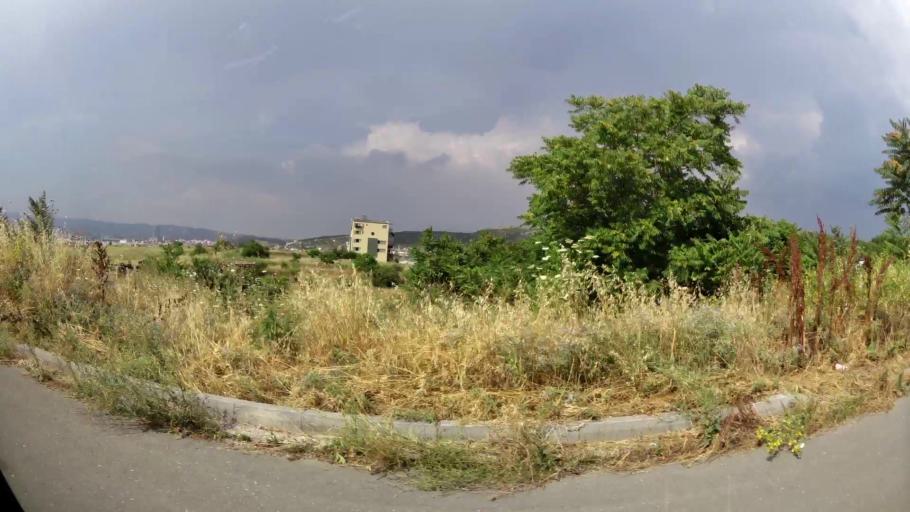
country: GR
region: Central Macedonia
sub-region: Nomos Thessalonikis
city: Polichni
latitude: 40.6682
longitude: 22.9535
